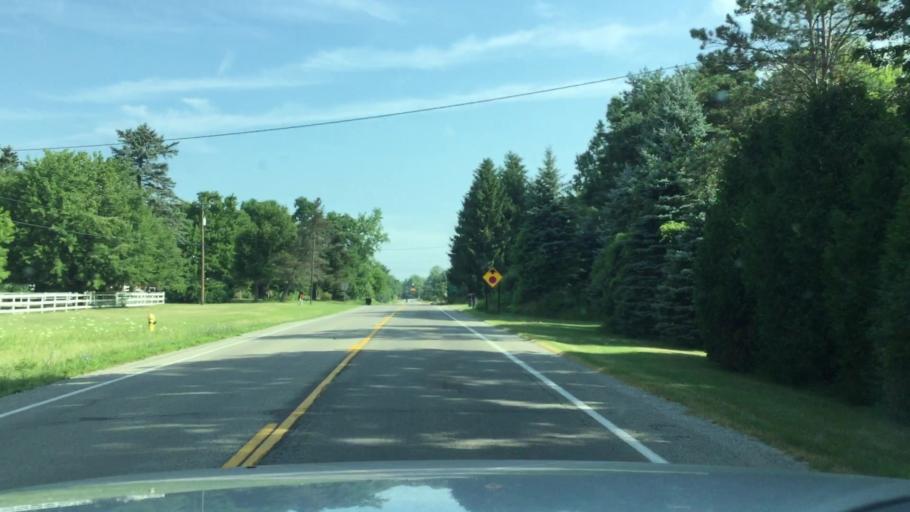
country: US
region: Michigan
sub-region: Genesee County
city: Flushing
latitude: 43.1151
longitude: -83.8728
